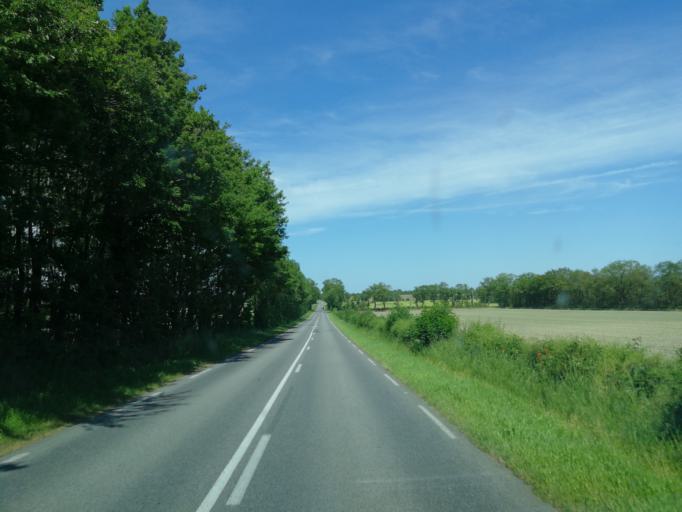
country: FR
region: Poitou-Charentes
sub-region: Departement des Deux-Sevres
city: Saint-Varent
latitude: 46.8877
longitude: -0.3104
